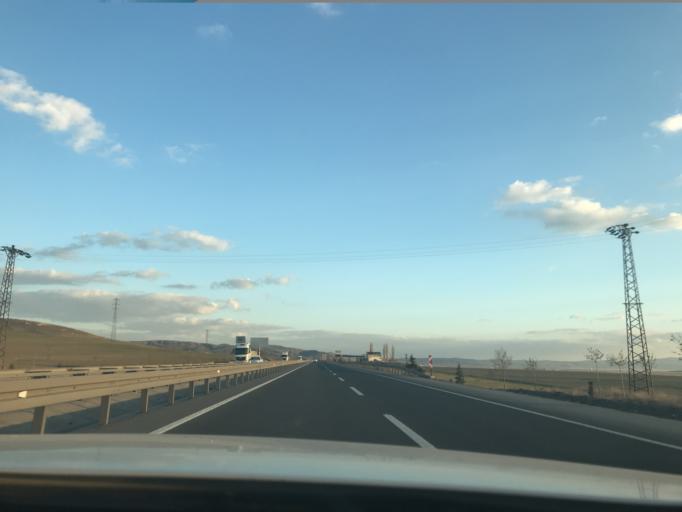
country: TR
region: Ankara
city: Altpinar
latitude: 39.3867
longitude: 32.8886
